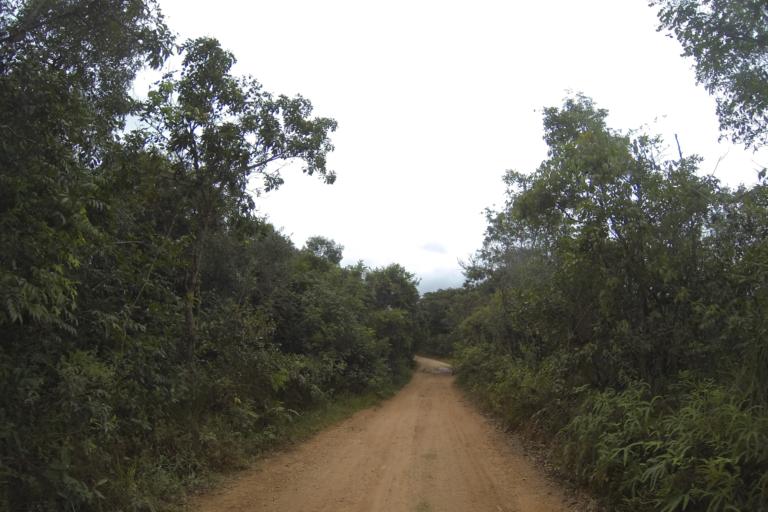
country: BR
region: Minas Gerais
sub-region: Ibia
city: Ibia
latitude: -19.7443
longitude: -46.5536
